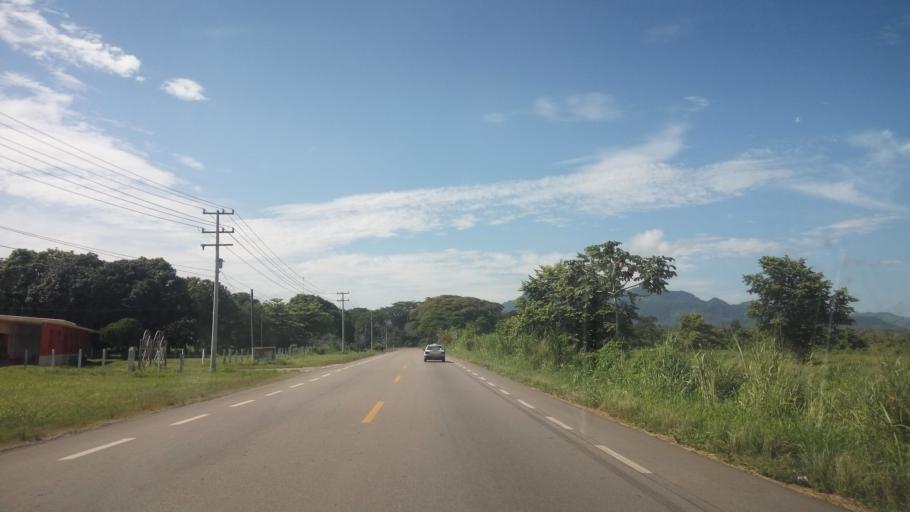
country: MX
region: Tabasco
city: Teapa
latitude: 17.5860
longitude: -92.9676
